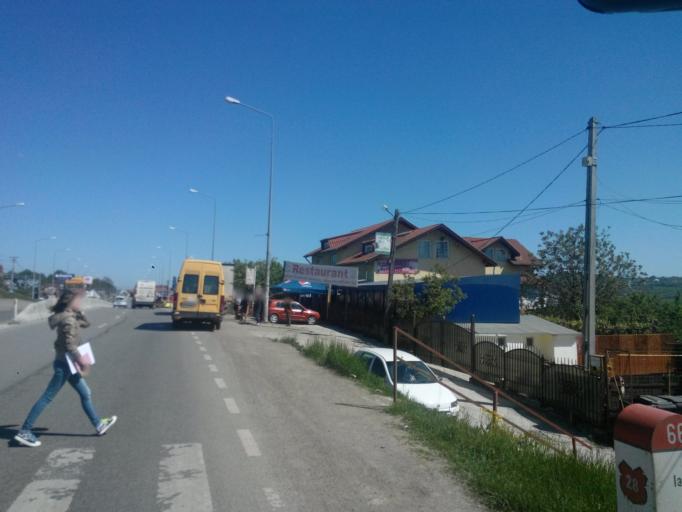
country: RO
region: Iasi
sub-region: Comuna Valea Lupului
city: Valea Lupului
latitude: 47.1751
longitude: 27.4988
